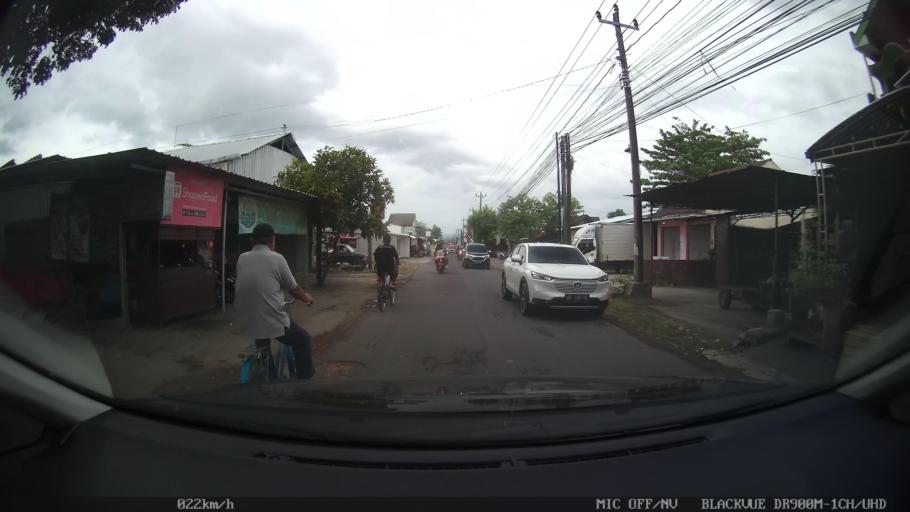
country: ID
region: Daerah Istimewa Yogyakarta
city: Sewon
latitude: -7.8356
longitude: 110.4120
